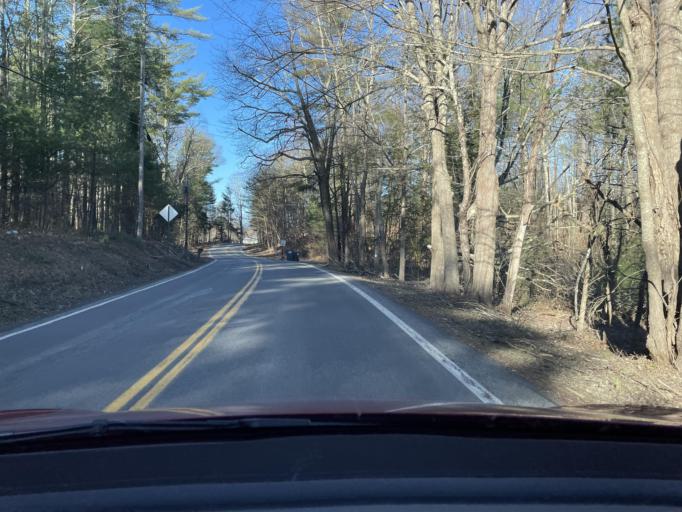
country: US
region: New York
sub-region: Ulster County
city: Zena
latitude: 42.0464
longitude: -74.0398
